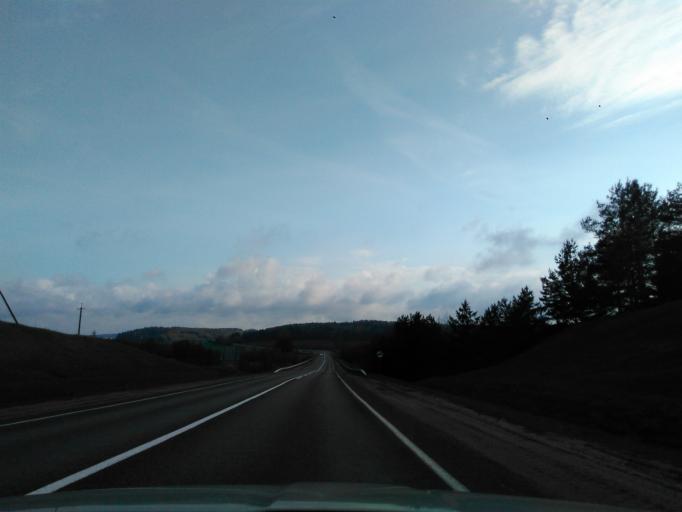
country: BY
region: Minsk
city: Lahoysk
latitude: 54.2362
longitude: 27.8396
